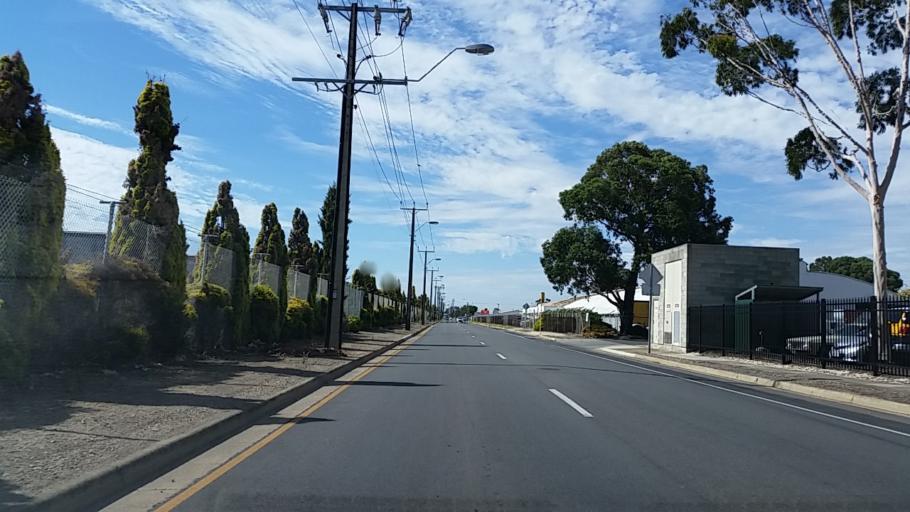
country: AU
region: South Australia
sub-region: Charles Sturt
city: Woodville North
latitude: -34.8592
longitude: 138.5385
